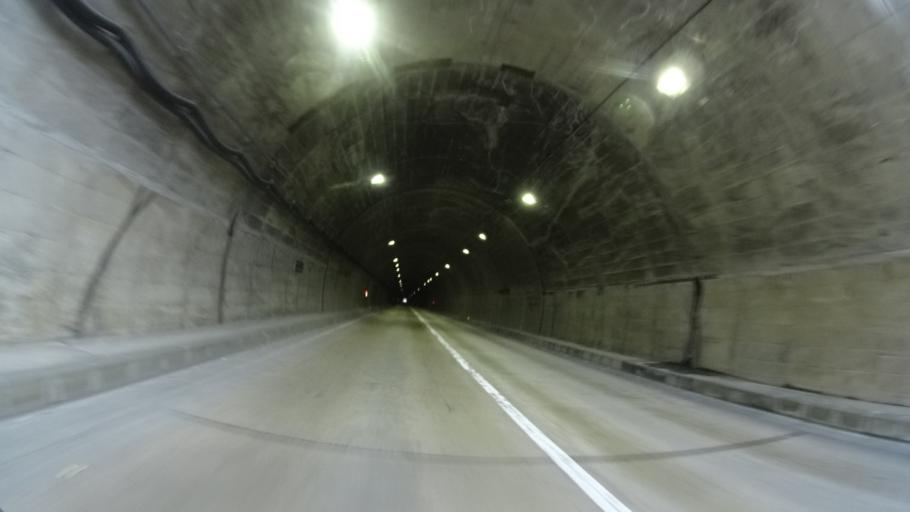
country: JP
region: Fukui
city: Maruoka
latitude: 36.1258
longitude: 136.3229
